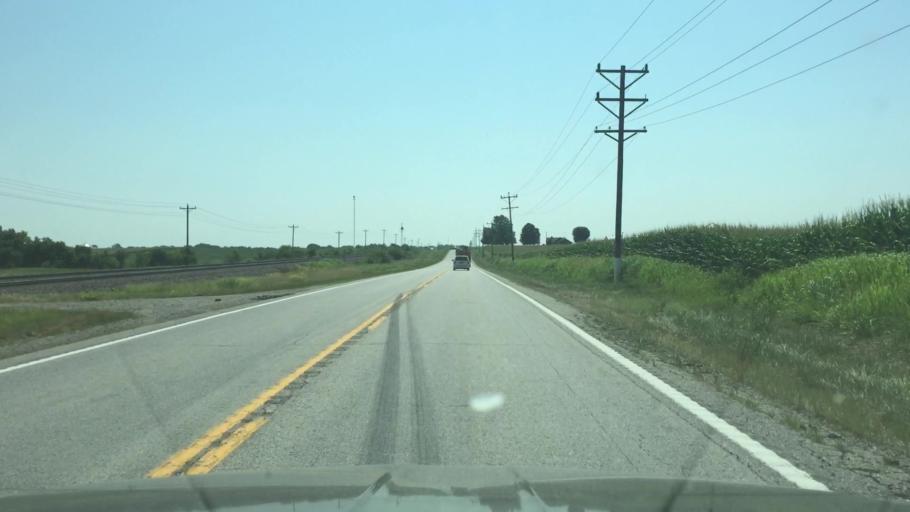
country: US
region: Missouri
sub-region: Moniteau County
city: Tipton
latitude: 38.6656
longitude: -92.8338
